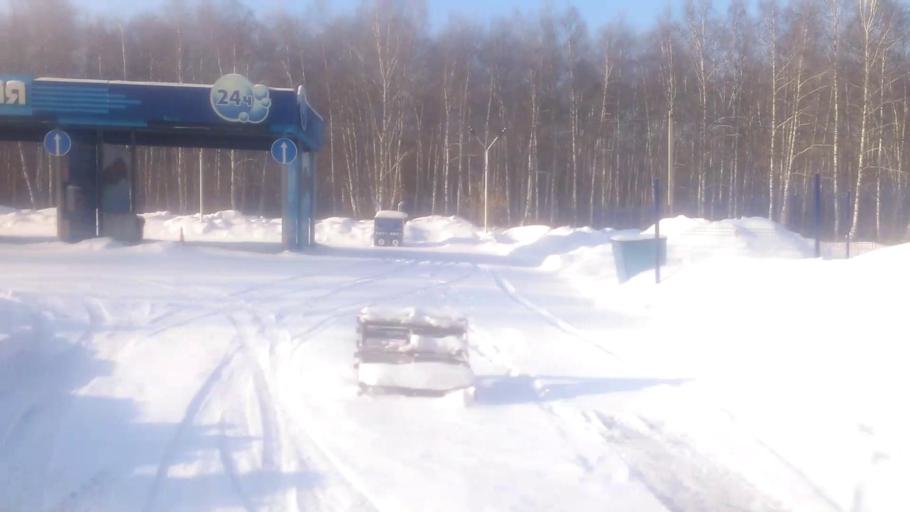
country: RU
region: Altai Krai
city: Novosilikatnyy
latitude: 53.3716
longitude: 83.6622
